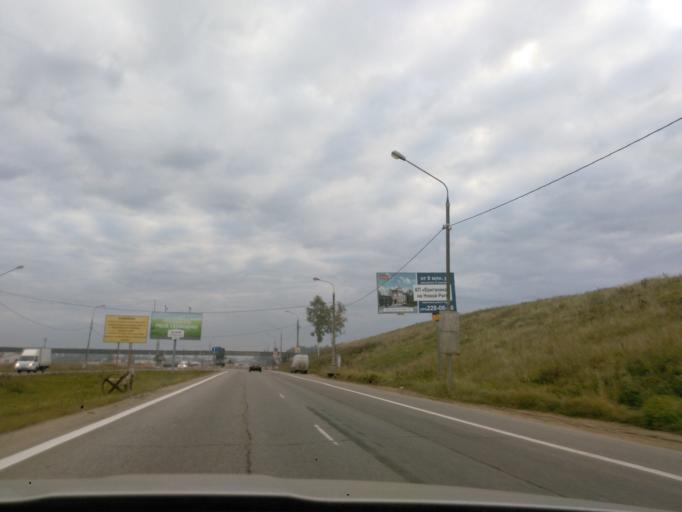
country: RU
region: Moskovskaya
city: Novopodrezkovo
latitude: 55.9693
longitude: 37.3720
